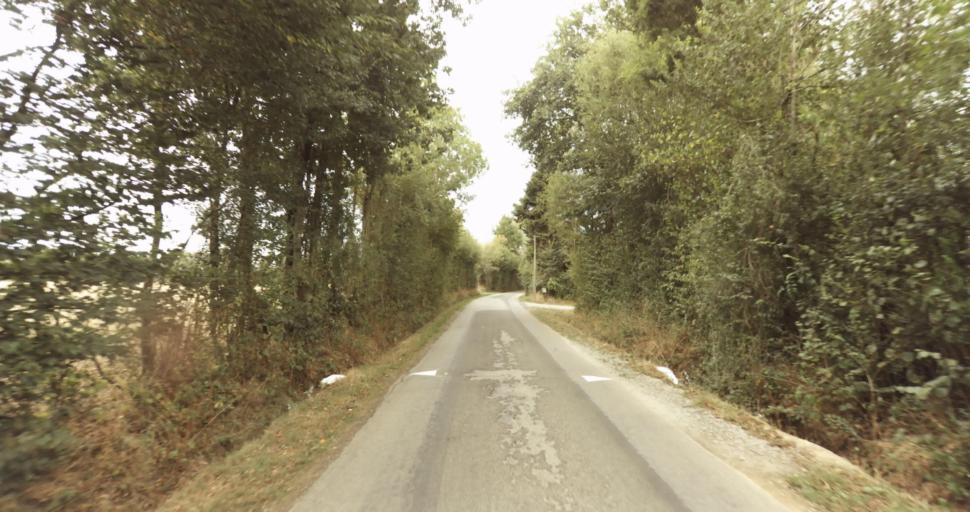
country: FR
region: Lower Normandy
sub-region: Departement du Calvados
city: Orbec
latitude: 48.9070
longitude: 0.3564
